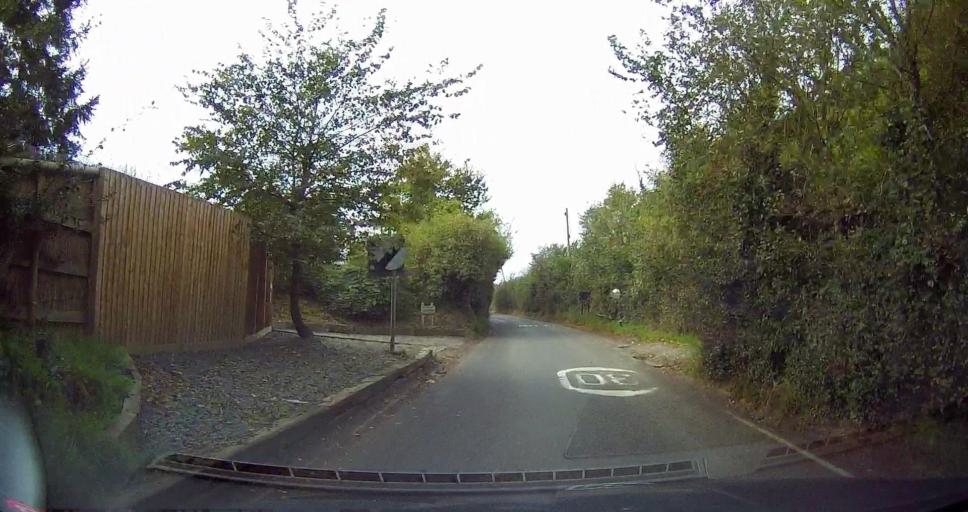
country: GB
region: England
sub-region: Kent
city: Longfield
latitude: 51.4202
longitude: 0.3036
